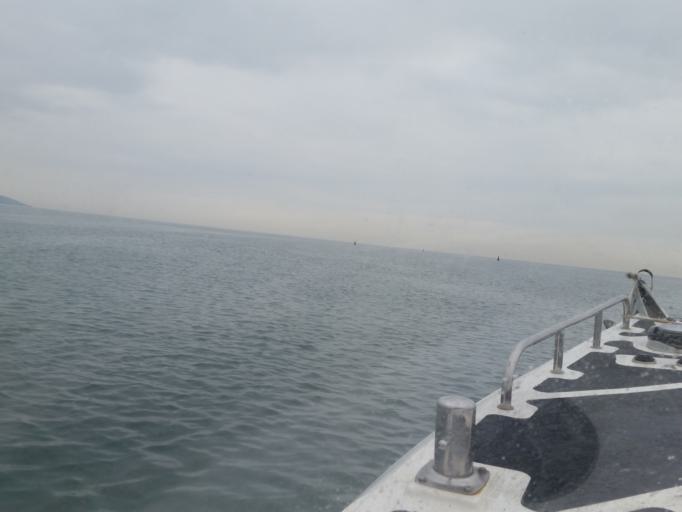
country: IE
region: Leinster
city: Malahide
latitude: 53.4513
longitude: -6.1320
